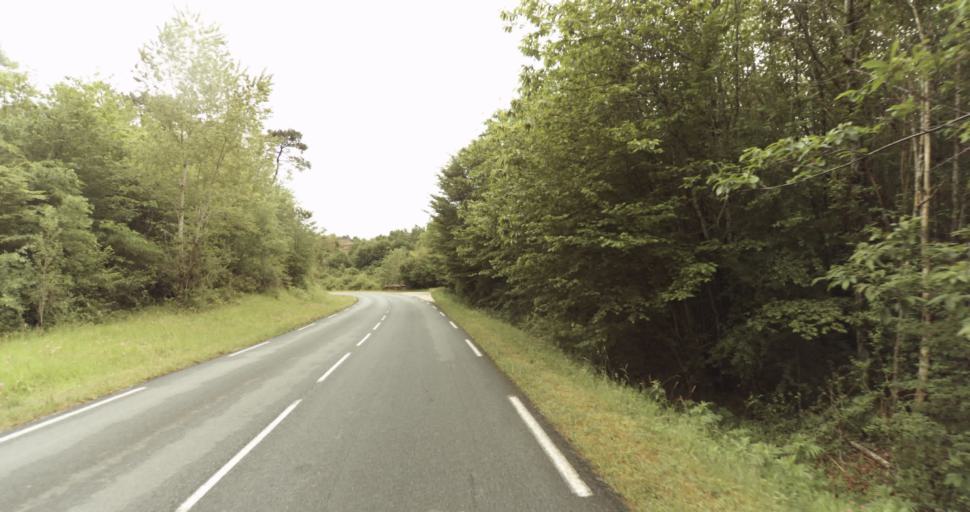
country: FR
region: Aquitaine
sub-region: Departement de la Dordogne
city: Belves
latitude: 44.6667
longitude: 1.0058
